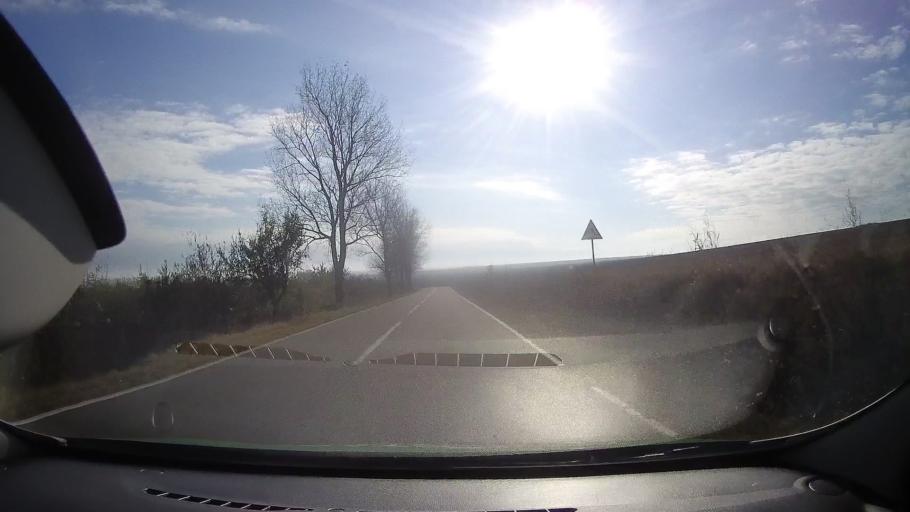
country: RO
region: Tulcea
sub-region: Comuna Mahmudia
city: Mahmudia
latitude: 45.0734
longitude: 29.0923
